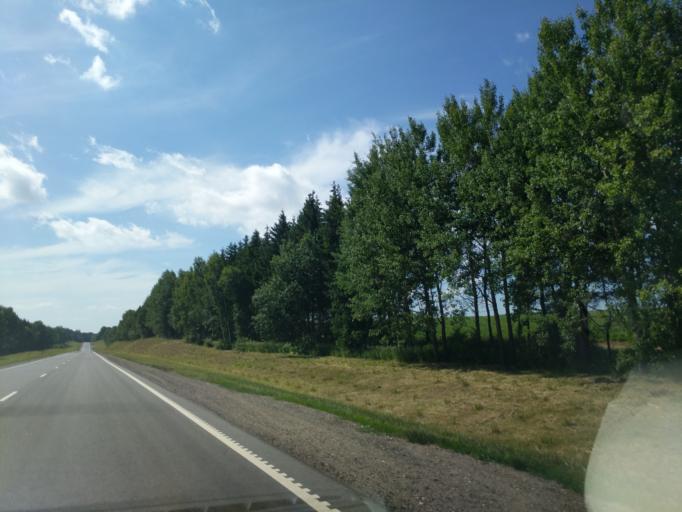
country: BY
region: Minsk
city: Syomkava
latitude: 54.1154
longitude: 27.4183
